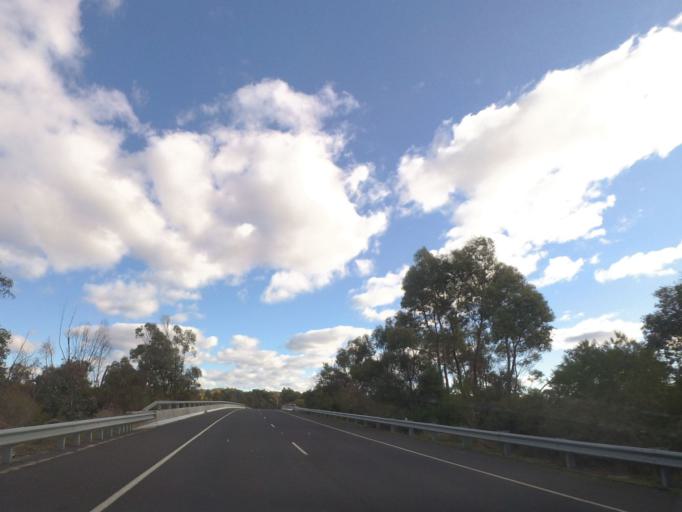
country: AU
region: Victoria
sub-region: Mount Alexander
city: Castlemaine
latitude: -37.1016
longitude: 144.3203
